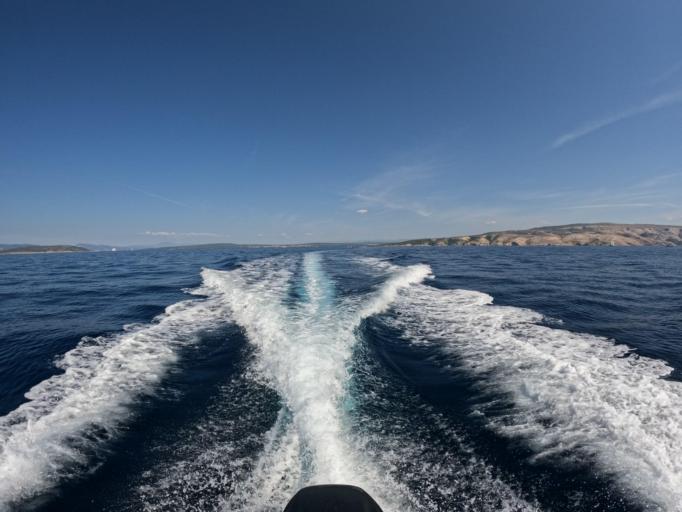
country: HR
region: Primorsko-Goranska
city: Punat
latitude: 44.9366
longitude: 14.6162
